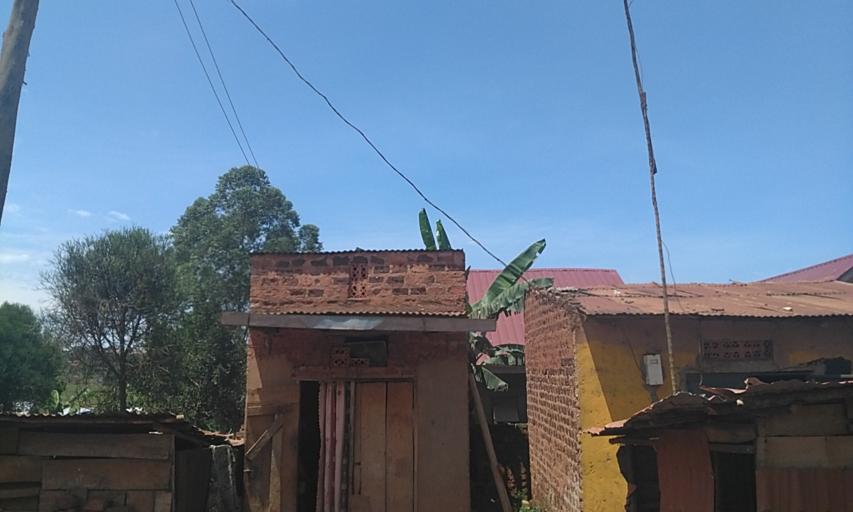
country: UG
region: Central Region
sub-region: Wakiso District
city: Wakiso
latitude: 0.4100
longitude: 32.4737
